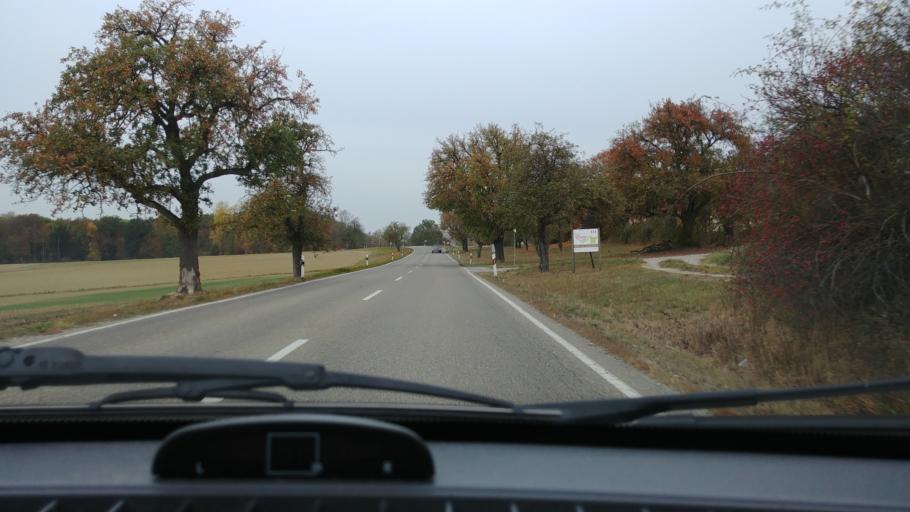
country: DE
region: Baden-Wuerttemberg
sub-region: Regierungsbezirk Stuttgart
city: Wallhausen
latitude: 49.2158
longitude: 10.0610
